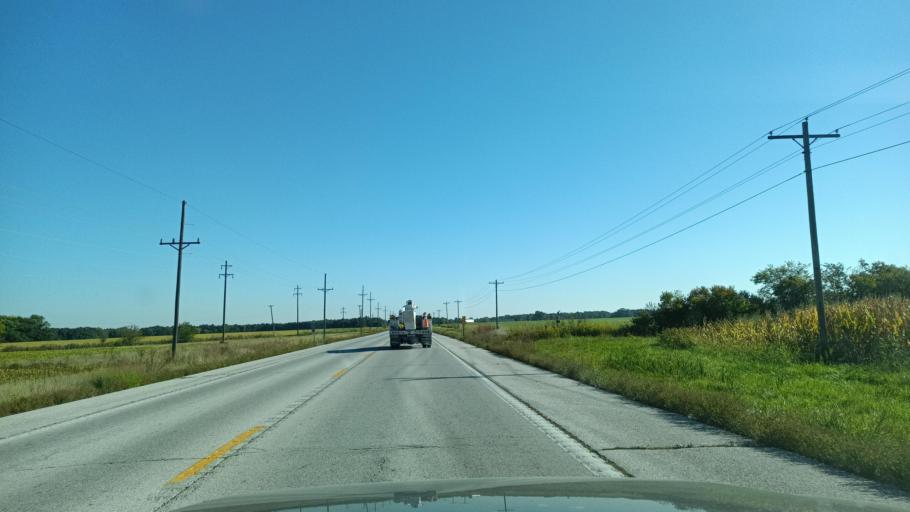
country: US
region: Missouri
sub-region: Audrain County
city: Vandalia
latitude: 39.4534
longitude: -91.6222
